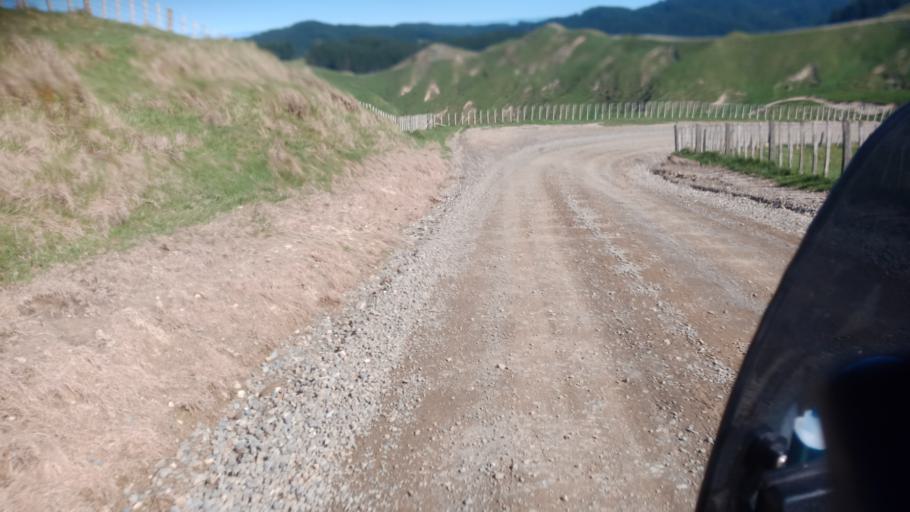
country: NZ
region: Gisborne
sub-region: Gisborne District
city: Gisborne
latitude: -39.1651
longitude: 177.9005
